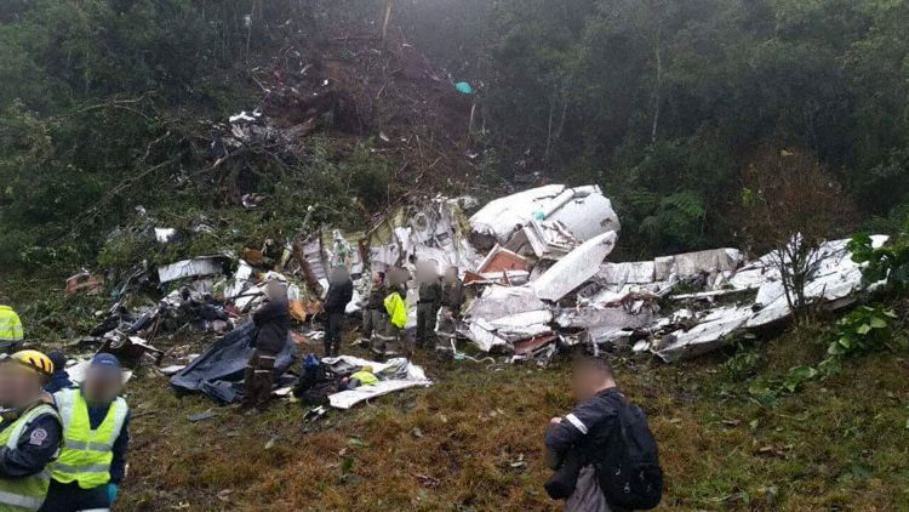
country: CO
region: Antioquia
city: La Ceja
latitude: 5.9814
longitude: -75.4198
